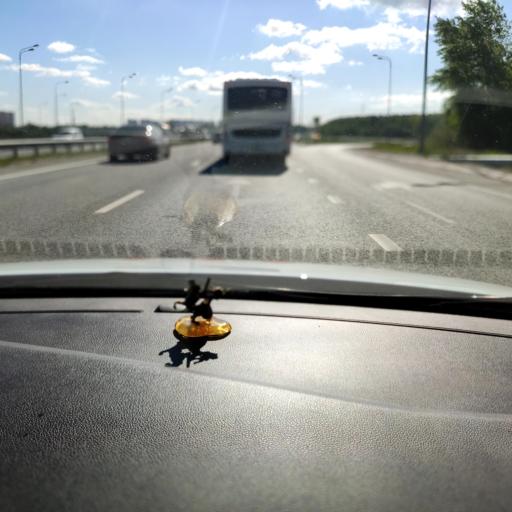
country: RU
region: Tatarstan
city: Osinovo
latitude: 55.8585
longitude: 48.8480
